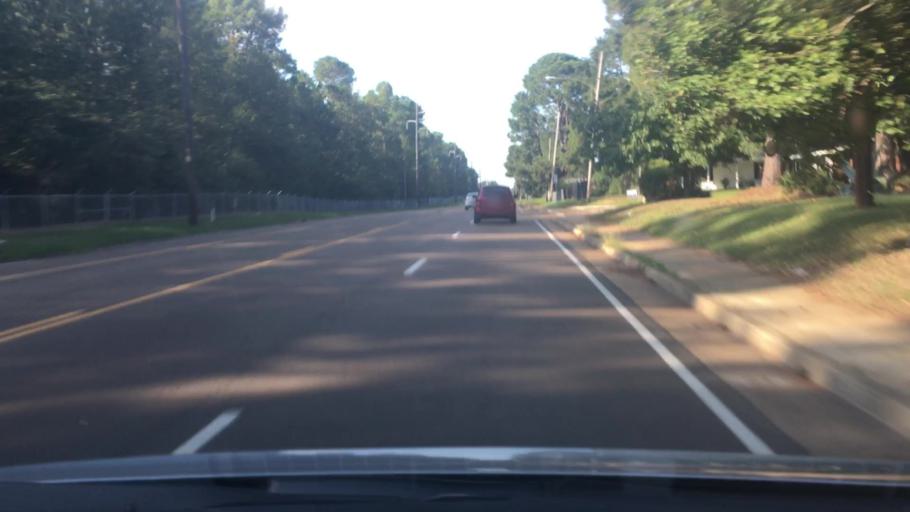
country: US
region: Mississippi
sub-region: Hinds County
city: Jackson
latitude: 32.3623
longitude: -90.1926
